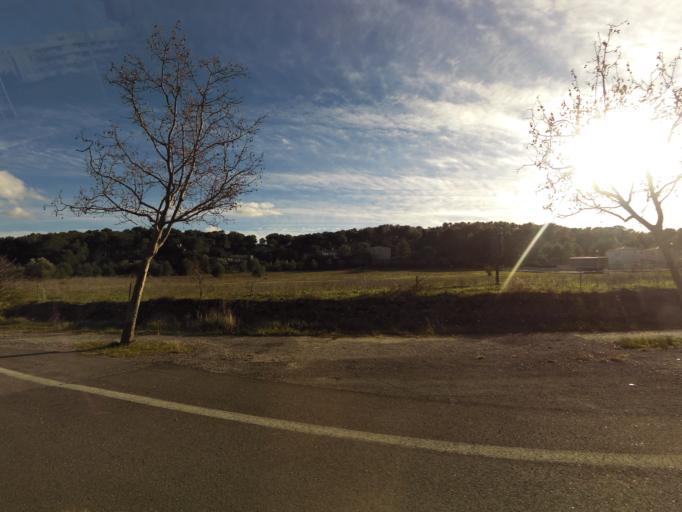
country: FR
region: Languedoc-Roussillon
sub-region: Departement du Gard
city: Caveirac
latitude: 43.8230
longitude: 4.2728
